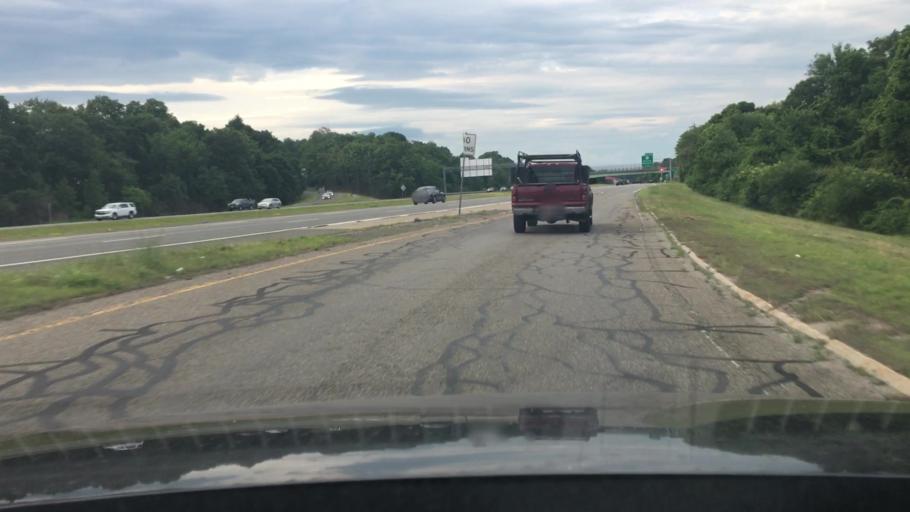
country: US
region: Massachusetts
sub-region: Essex County
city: Danvers
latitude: 42.5643
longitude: -70.9715
